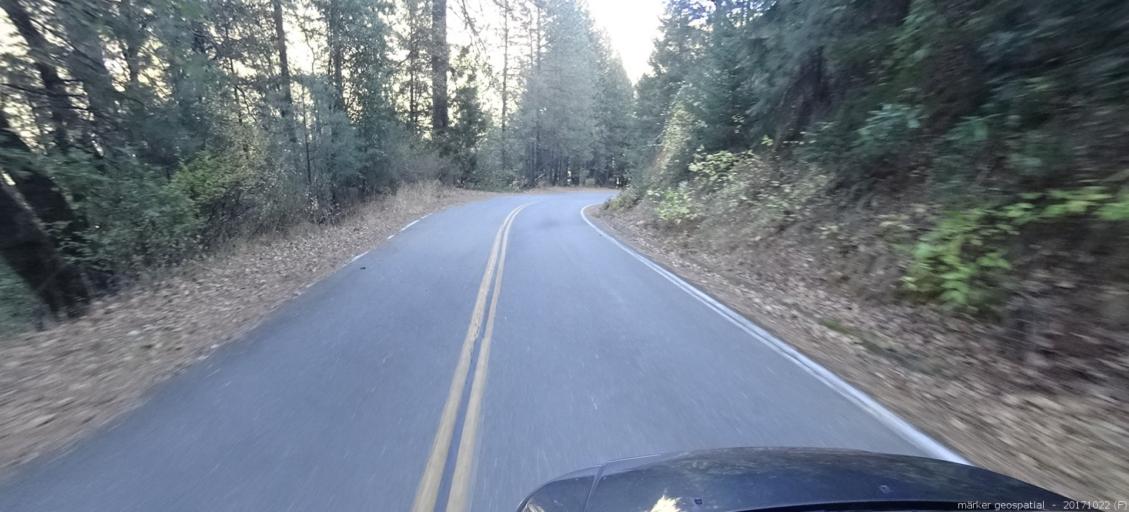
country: US
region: California
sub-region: Shasta County
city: Shasta Lake
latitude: 40.9109
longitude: -122.2379
